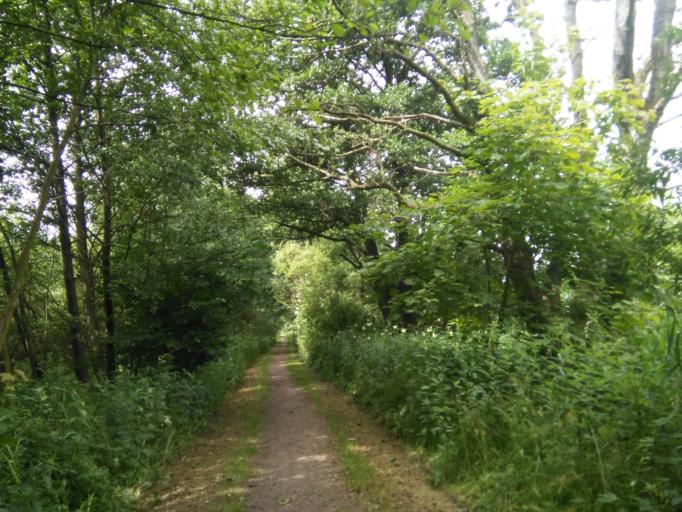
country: DK
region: Central Jutland
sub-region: Horsens Kommune
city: Horsens
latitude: 55.8753
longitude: 9.8619
